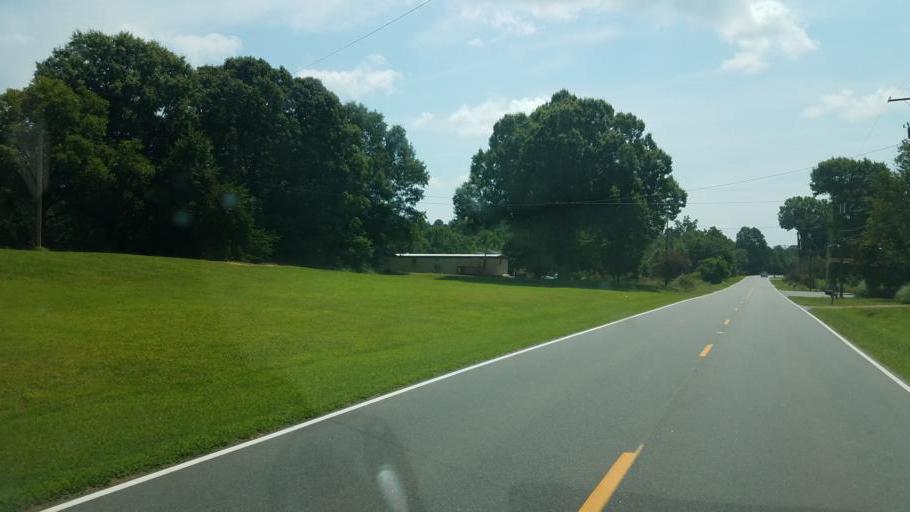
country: US
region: North Carolina
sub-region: Gaston County
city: Cherryville
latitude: 35.3678
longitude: -81.3711
